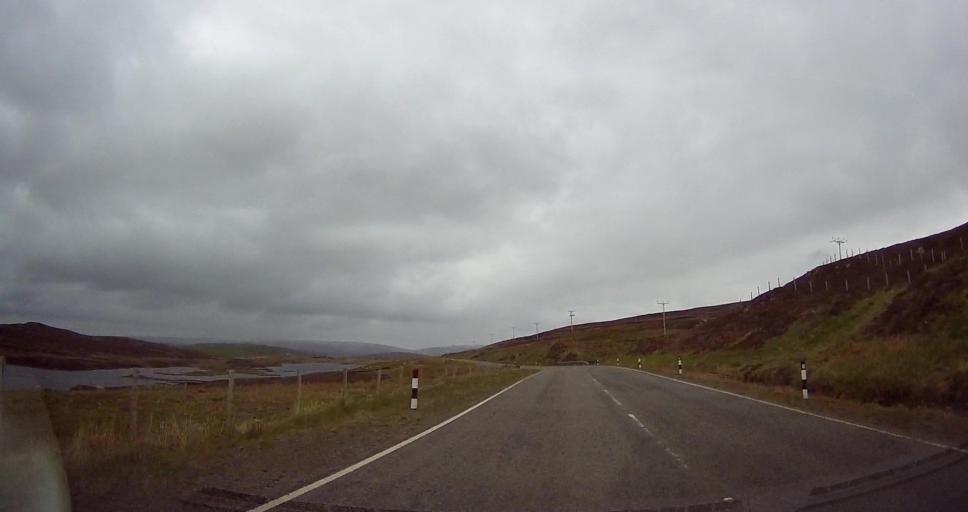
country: GB
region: Scotland
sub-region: Shetland Islands
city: Sandwick
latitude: 60.2589
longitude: -1.4828
